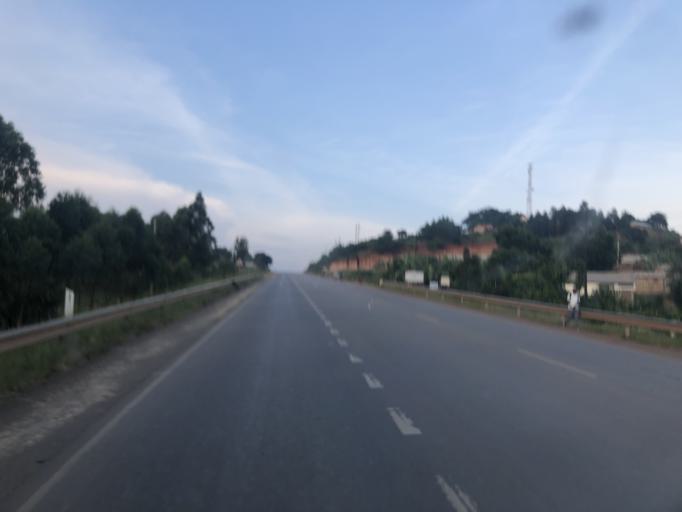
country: UG
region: Central Region
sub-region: Mpigi District
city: Mpigi
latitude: 0.2157
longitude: 32.3279
